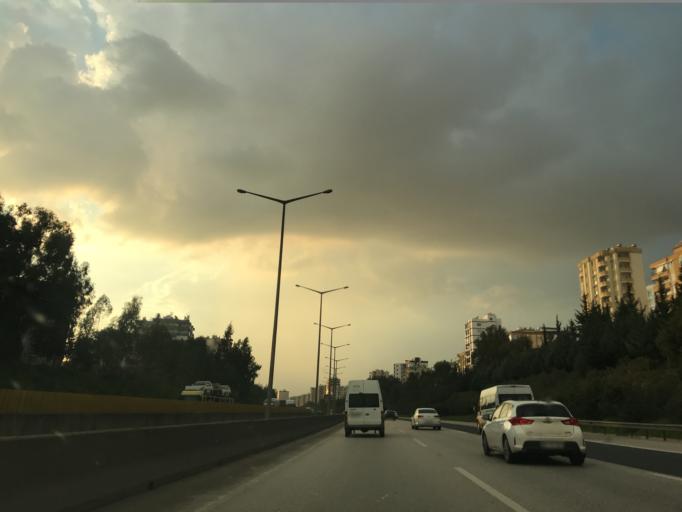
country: TR
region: Adana
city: Adana
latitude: 37.0315
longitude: 35.3083
